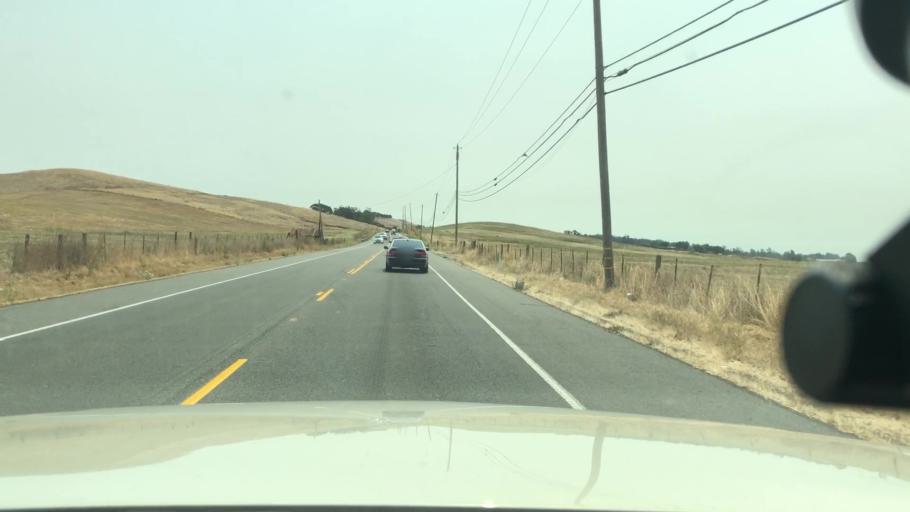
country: US
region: California
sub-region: Sonoma County
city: Petaluma
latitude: 38.2206
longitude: -122.5648
